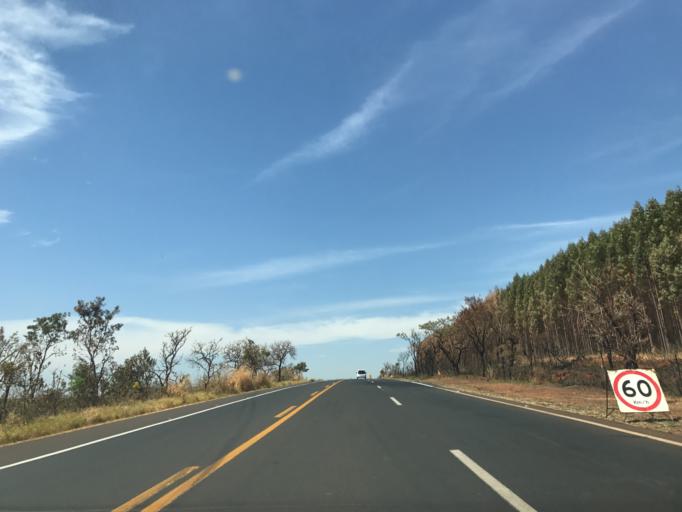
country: BR
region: Minas Gerais
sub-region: Prata
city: Prata
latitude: -19.1212
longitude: -48.9683
